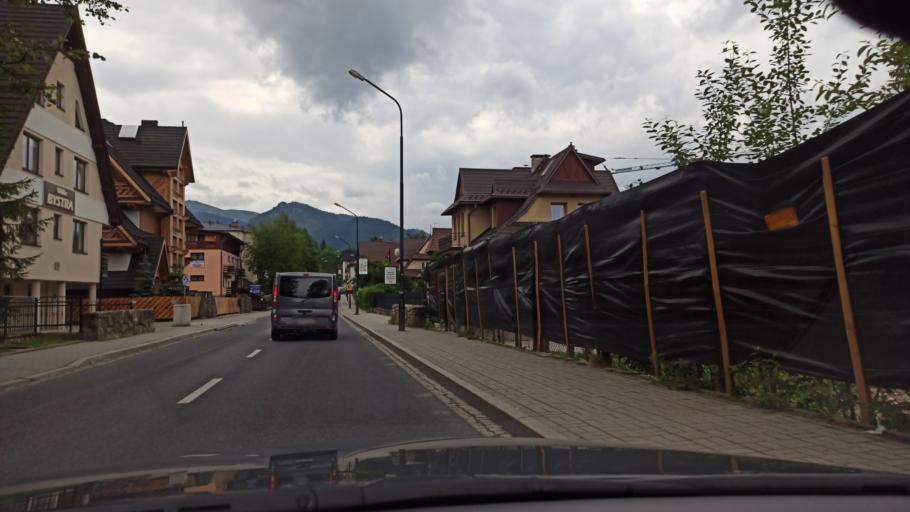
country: PL
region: Lesser Poland Voivodeship
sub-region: Powiat tatrzanski
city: Zakopane
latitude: 49.2874
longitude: 19.9583
